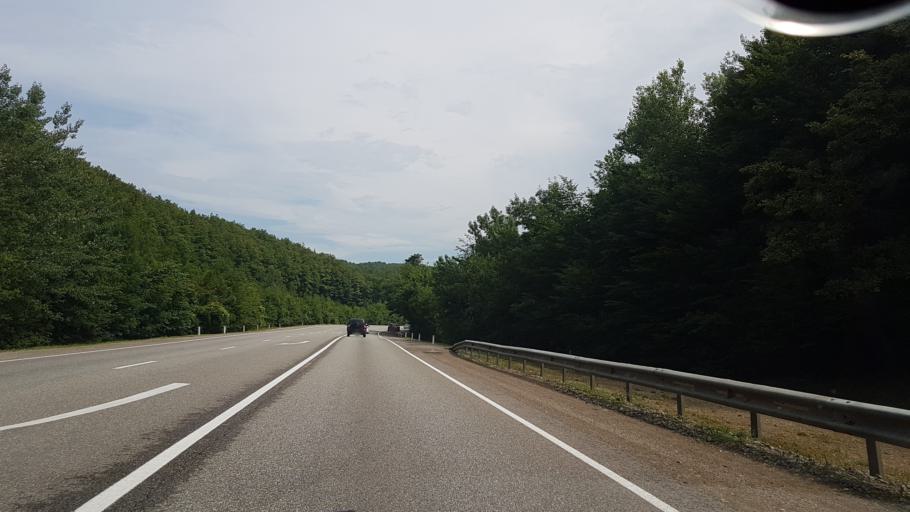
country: RU
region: Krasnodarskiy
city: Goryachiy Klyuch
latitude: 44.5357
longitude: 38.9484
